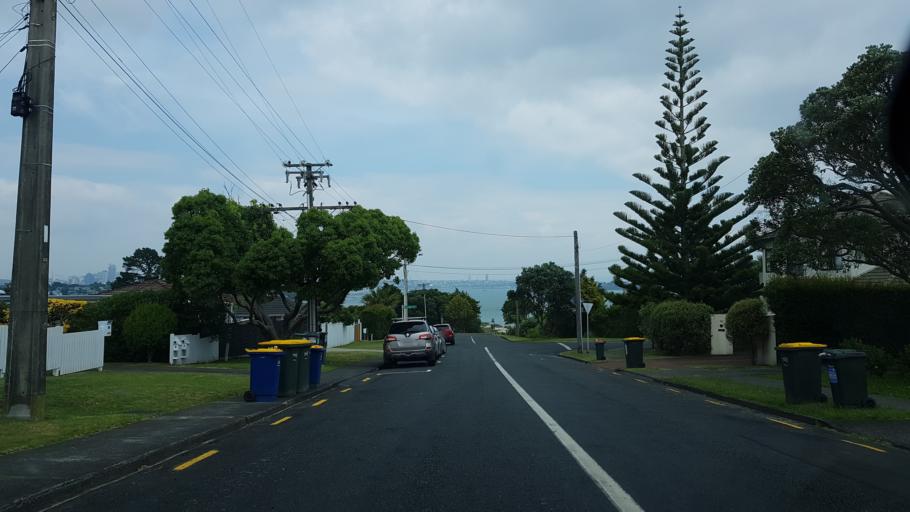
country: NZ
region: Auckland
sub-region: Auckland
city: North Shore
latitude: -36.8036
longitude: 174.7740
